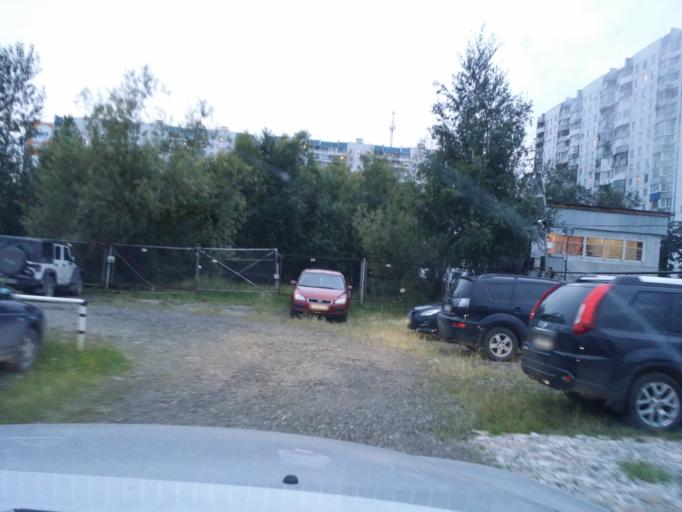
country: RU
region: Khanty-Mansiyskiy Avtonomnyy Okrug
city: Nizhnevartovsk
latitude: 60.9368
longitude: 76.5907
